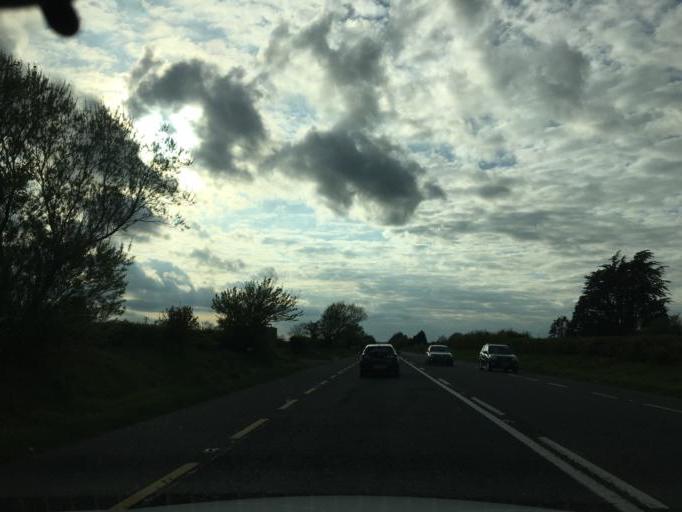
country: IE
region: Leinster
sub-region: Loch Garman
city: Loch Garman
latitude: 52.3432
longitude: -6.5830
